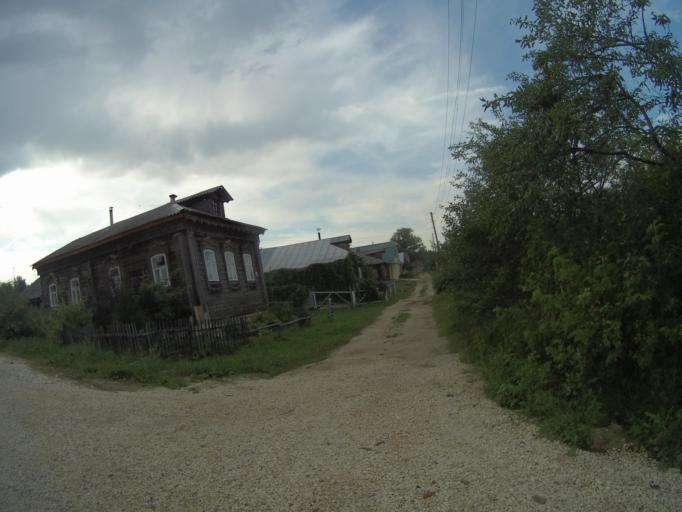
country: RU
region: Vladimir
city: Vorsha
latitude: 56.0142
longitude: 40.1803
